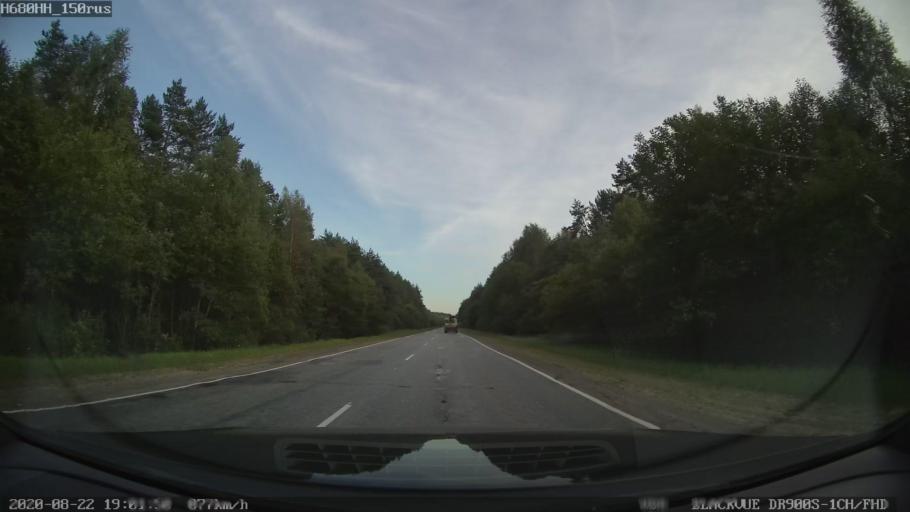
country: RU
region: Tverskaya
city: Vasil'yevskiy Mokh
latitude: 57.1150
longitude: 36.1171
